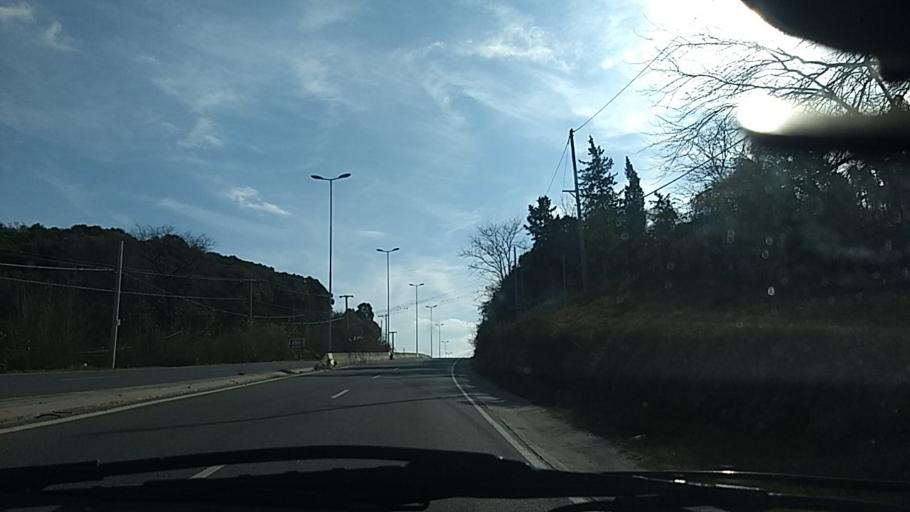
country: AR
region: Cordoba
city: Salsipuedes
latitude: -31.1519
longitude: -64.2991
